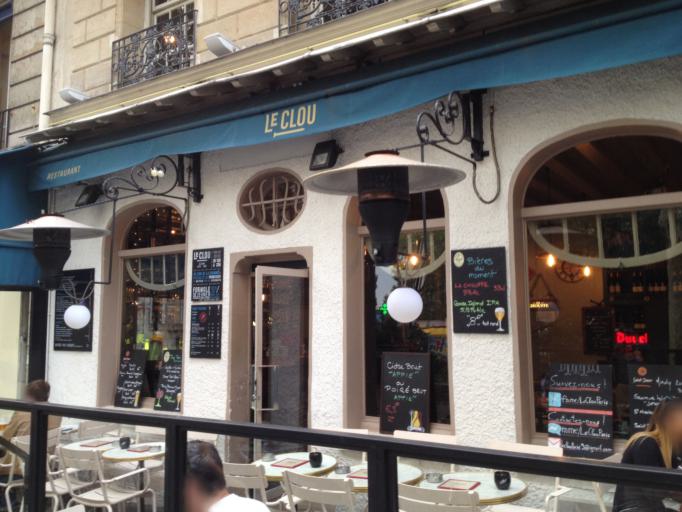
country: FR
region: Ile-de-France
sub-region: Paris
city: Saint-Ouen
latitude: 48.8809
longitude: 2.3405
